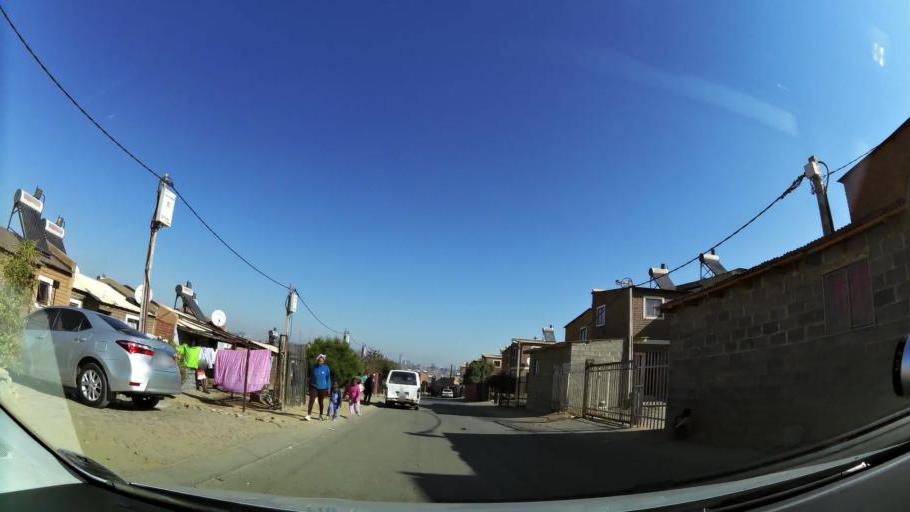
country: ZA
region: Gauteng
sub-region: City of Johannesburg Metropolitan Municipality
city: Modderfontein
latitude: -26.1067
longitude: 28.1183
